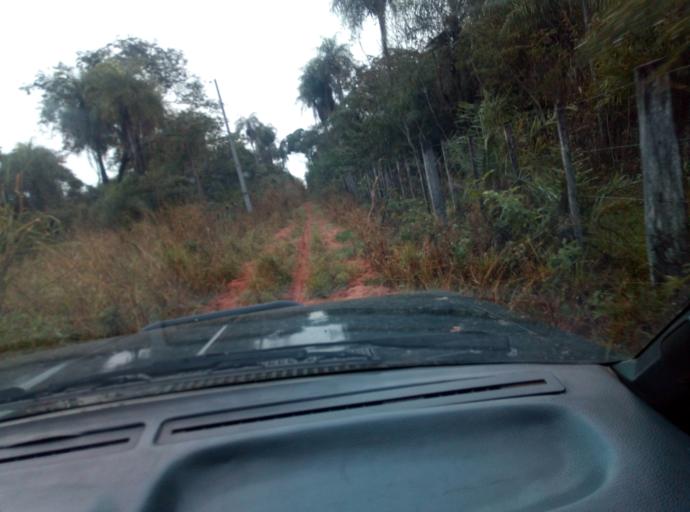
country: PY
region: Caaguazu
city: Carayao
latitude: -25.1925
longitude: -56.3544
